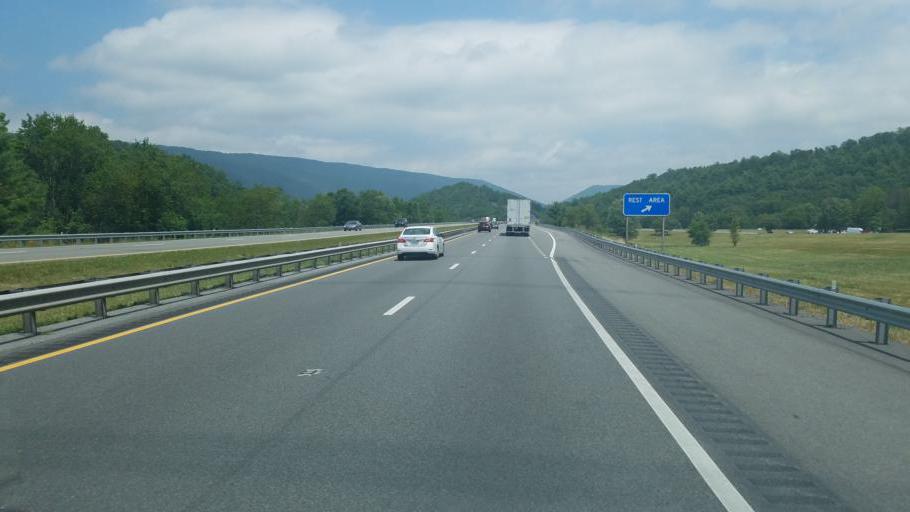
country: US
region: Virginia
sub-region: Bland County
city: Bland
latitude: 37.1844
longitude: -81.1326
